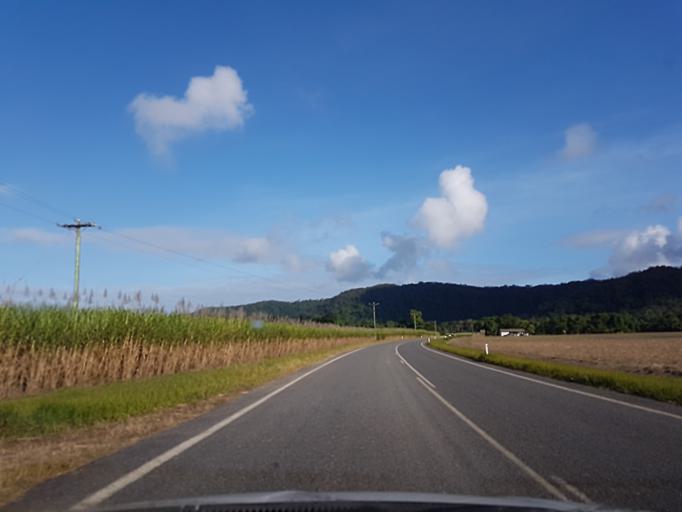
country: AU
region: Queensland
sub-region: Cairns
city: Port Douglas
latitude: -16.2977
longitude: 145.3896
